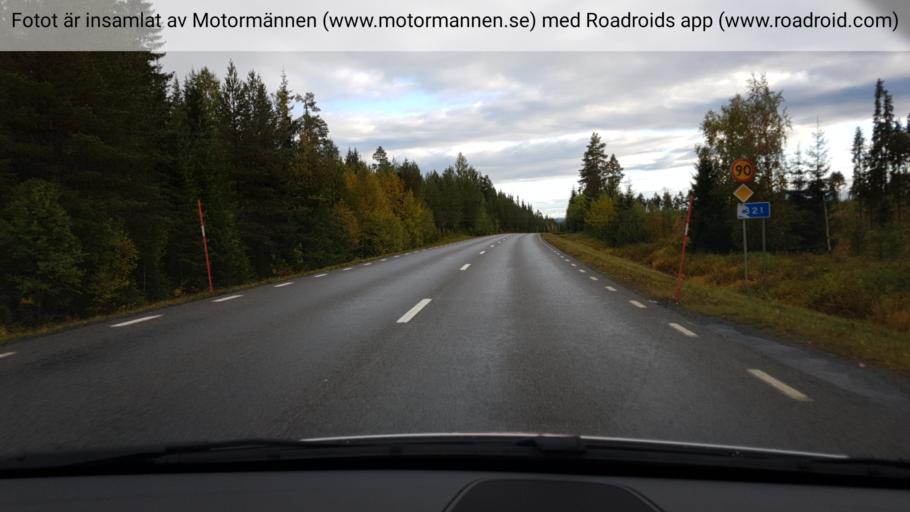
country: SE
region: Jaemtland
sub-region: Krokoms Kommun
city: Valla
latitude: 63.3041
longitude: 13.9247
